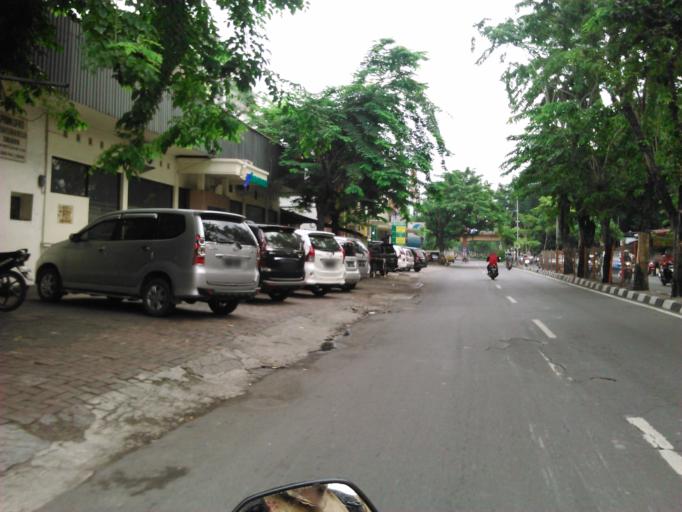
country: ID
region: East Java
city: Gubengairlangga
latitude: -7.2657
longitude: 112.7517
